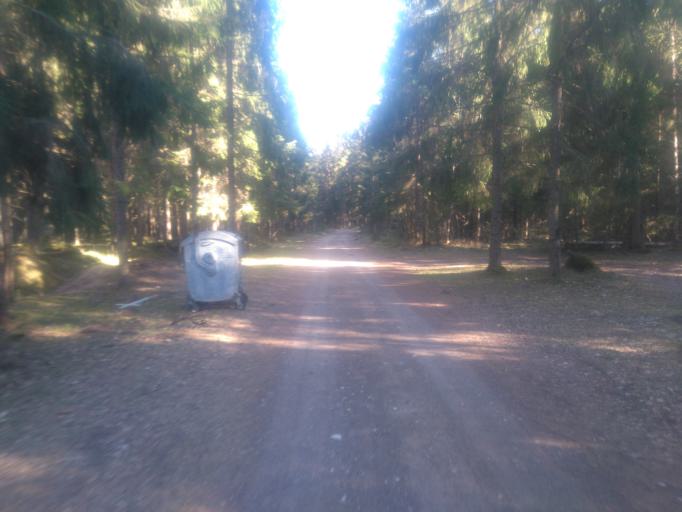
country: LV
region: Vecpiebalga
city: Vecpiebalga
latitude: 57.0099
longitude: 25.8414
